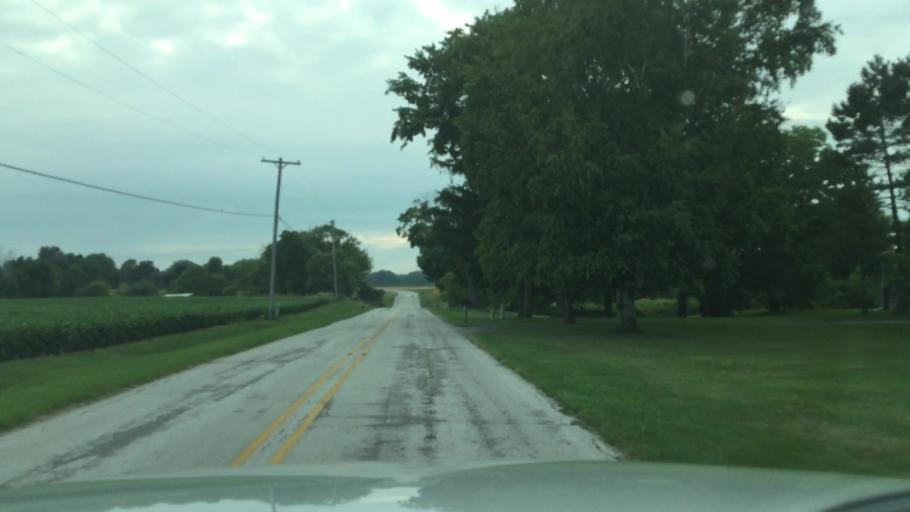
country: US
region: Michigan
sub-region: Saginaw County
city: Frankenmuth
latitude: 43.3333
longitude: -83.7820
